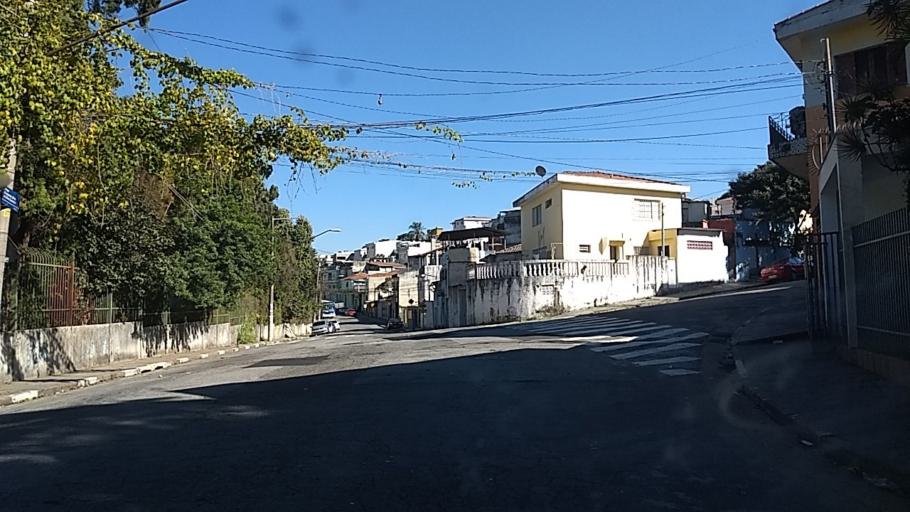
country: BR
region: Sao Paulo
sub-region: Guarulhos
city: Guarulhos
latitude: -23.5002
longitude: -46.5809
